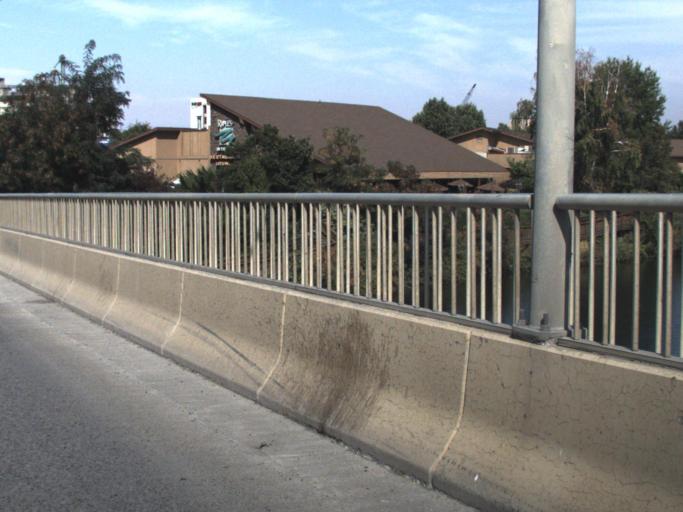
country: US
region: Washington
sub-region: Spokane County
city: Spokane
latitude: 47.6629
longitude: -117.4112
